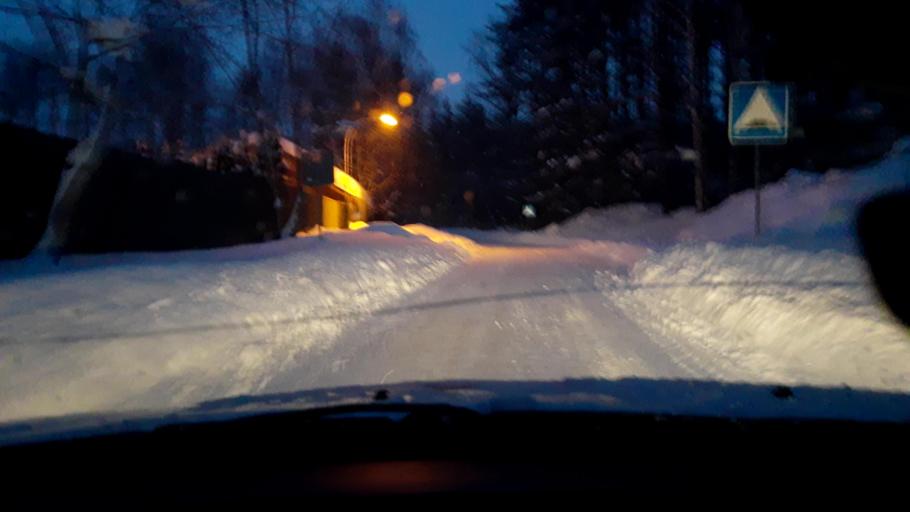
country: RU
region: Nizjnij Novgorod
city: Afonino
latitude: 56.1720
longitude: 44.0544
